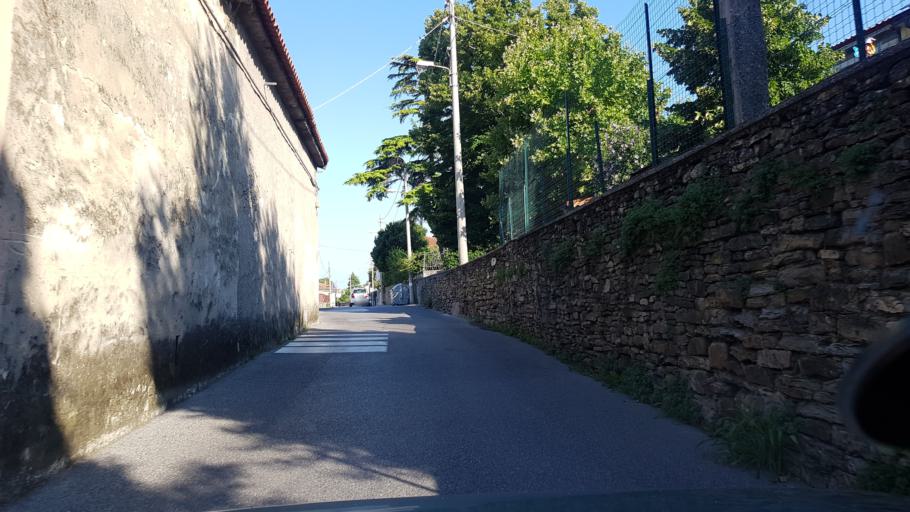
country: IT
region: Friuli Venezia Giulia
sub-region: Provincia di Trieste
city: Trieste
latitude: 45.6272
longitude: 13.8034
